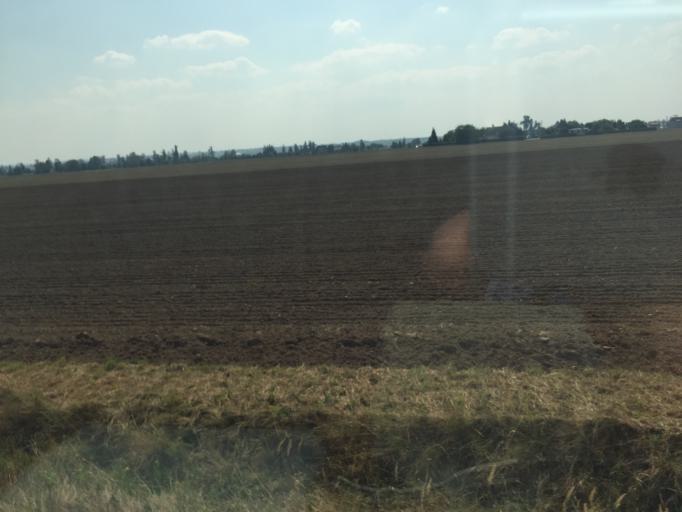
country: DE
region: Saxony
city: Grossenhain
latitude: 51.3020
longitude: 13.5611
